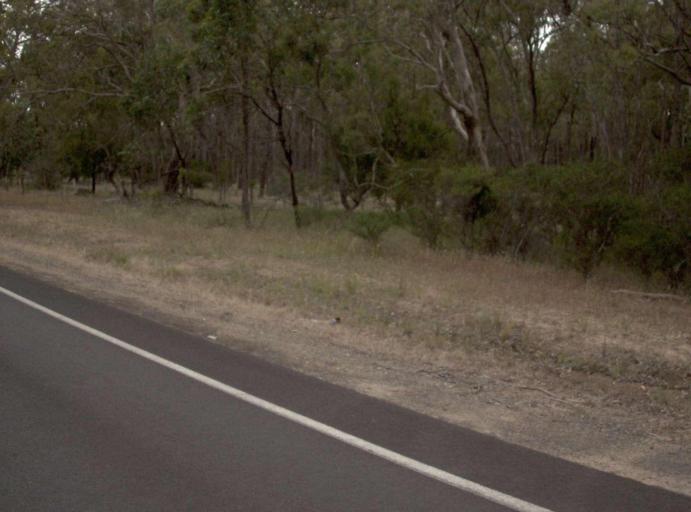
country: AU
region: Victoria
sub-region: Wellington
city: Sale
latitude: -38.4286
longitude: 146.9533
